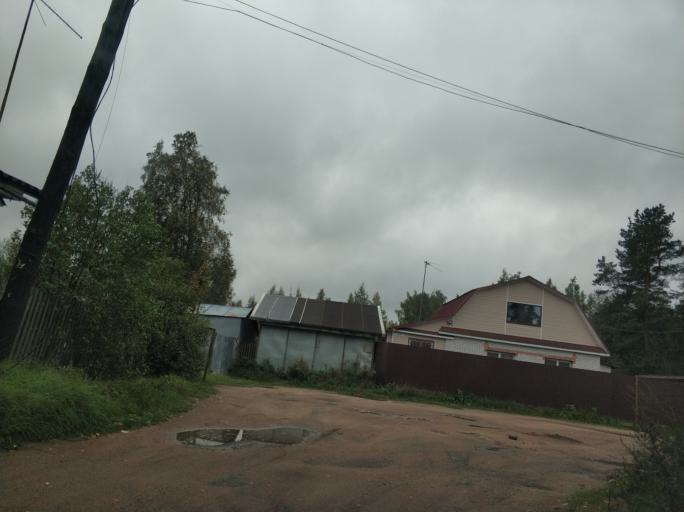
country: RU
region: Leningrad
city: Borisova Griva
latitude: 60.0848
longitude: 30.8868
